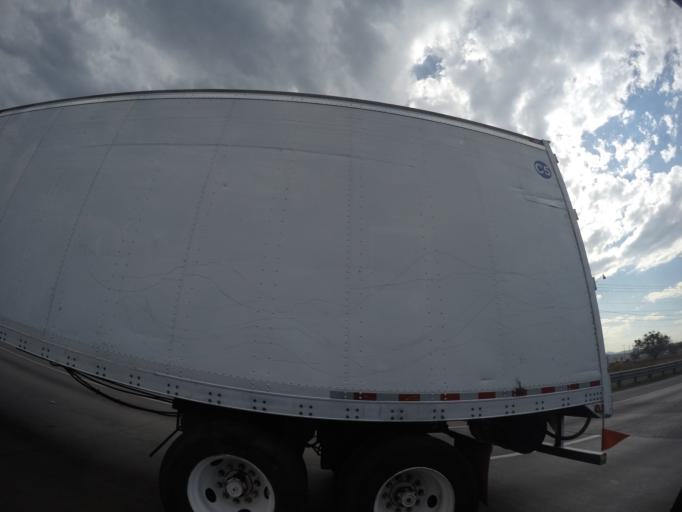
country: MX
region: Queretaro
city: La Estancia
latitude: 20.4259
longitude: -100.0549
